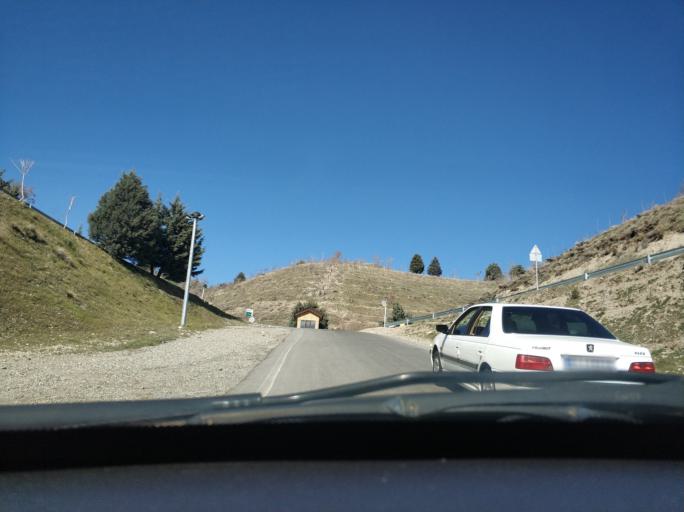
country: IR
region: Tehran
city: Tajrish
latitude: 35.7941
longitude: 51.5645
